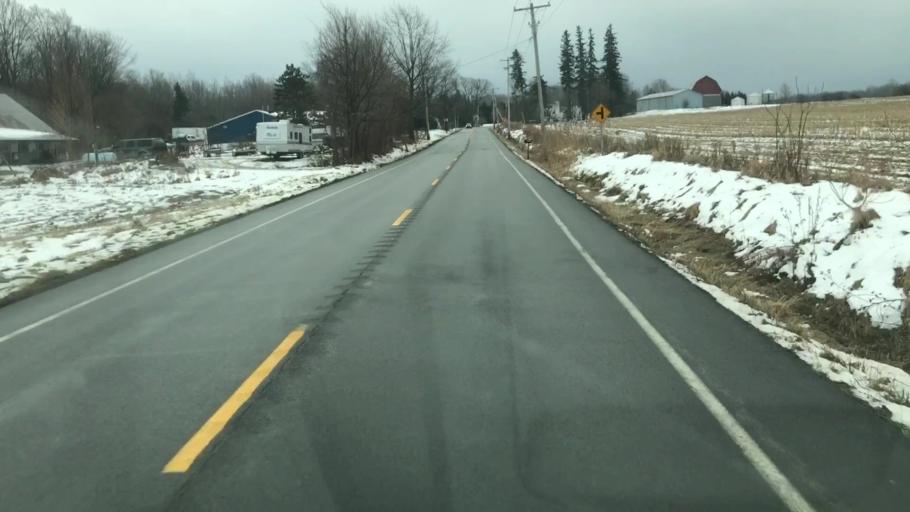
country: US
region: New York
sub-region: Cayuga County
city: Moravia
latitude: 42.8115
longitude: -76.3482
